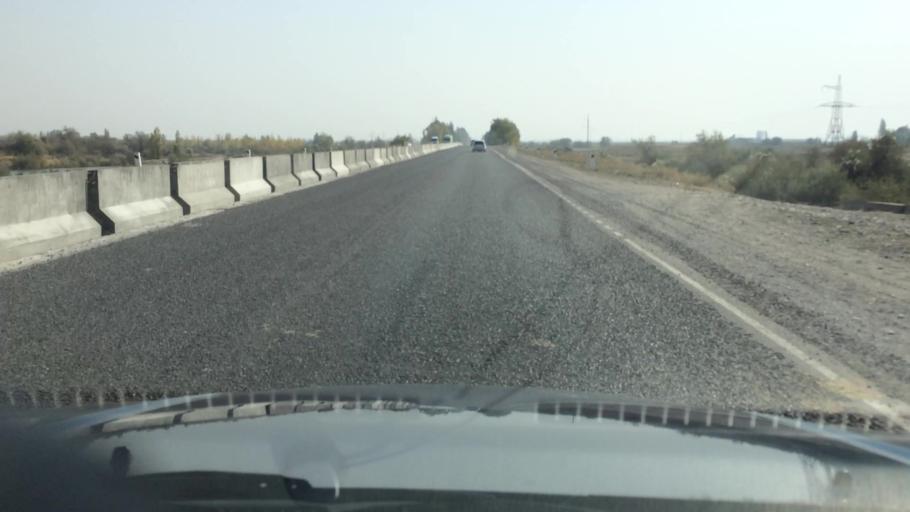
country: KG
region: Chuy
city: Kant
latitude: 42.9713
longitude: 74.9011
